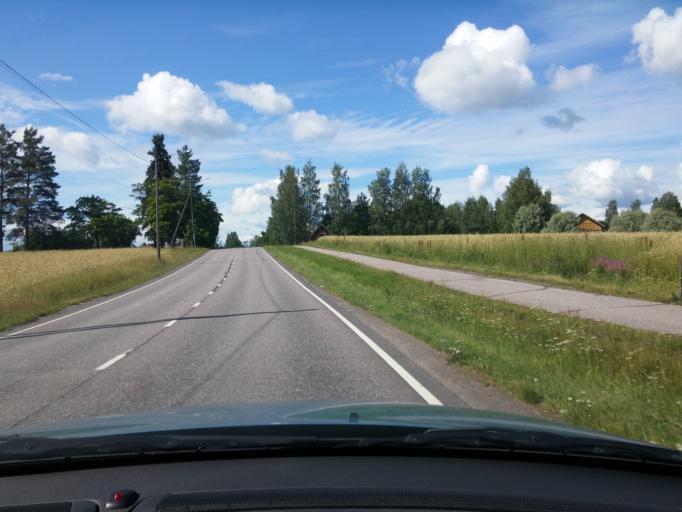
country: FI
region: Uusimaa
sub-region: Porvoo
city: Askola
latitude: 60.4952
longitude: 25.5437
